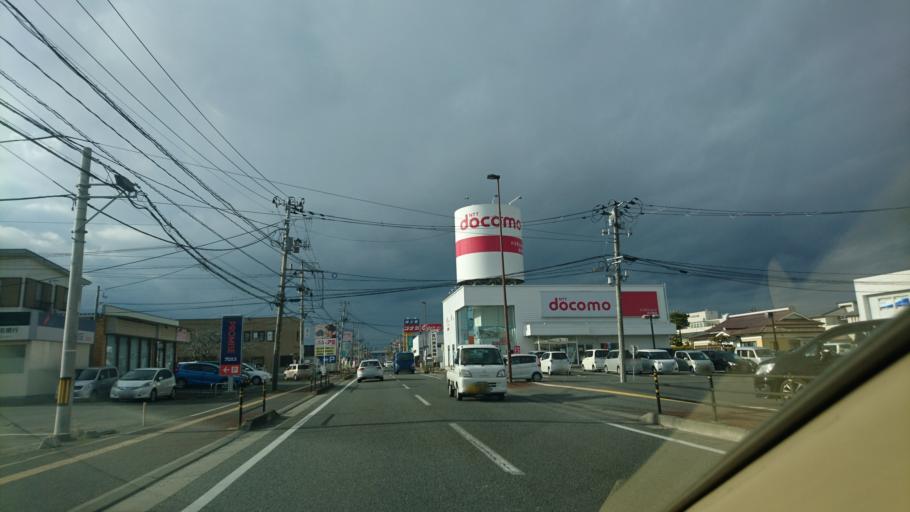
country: JP
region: Miyagi
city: Furukawa
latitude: 38.5714
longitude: 140.9765
